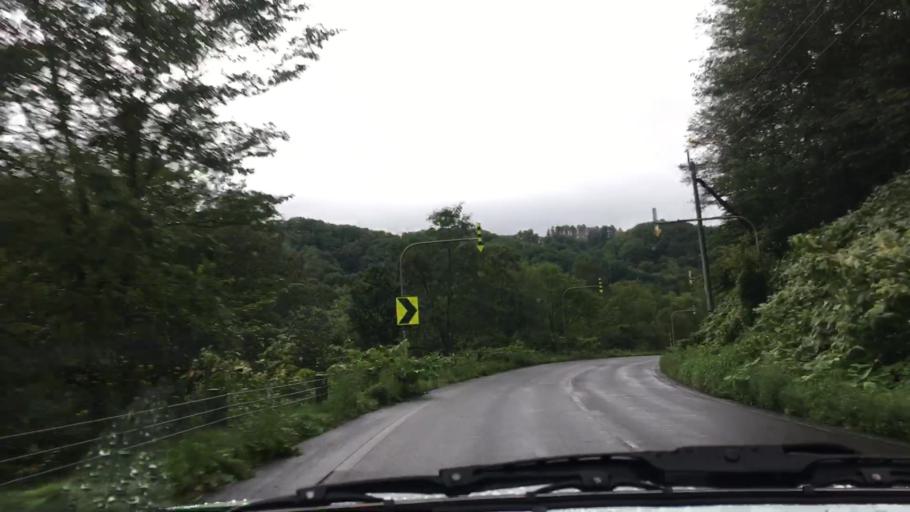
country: JP
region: Hokkaido
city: Niseko Town
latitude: 42.6668
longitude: 140.7777
